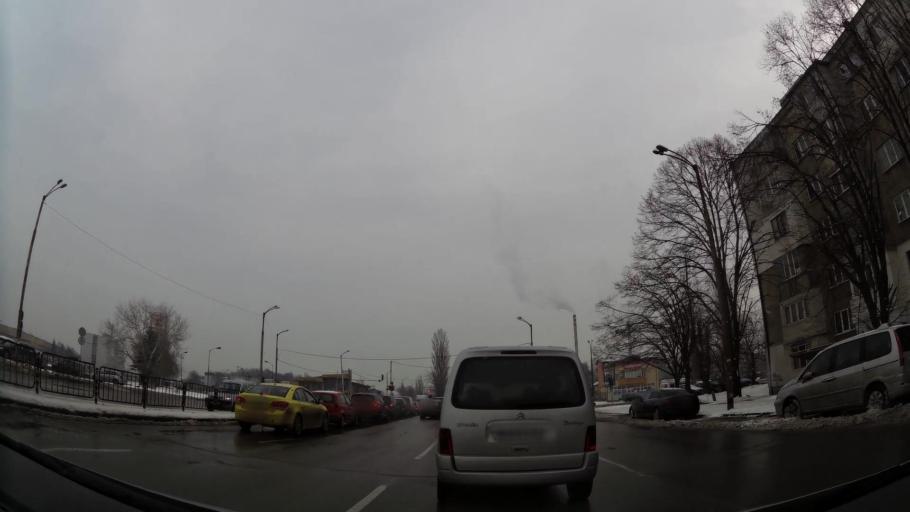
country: BG
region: Sofia-Capital
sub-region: Stolichna Obshtina
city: Sofia
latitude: 42.7112
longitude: 23.3537
